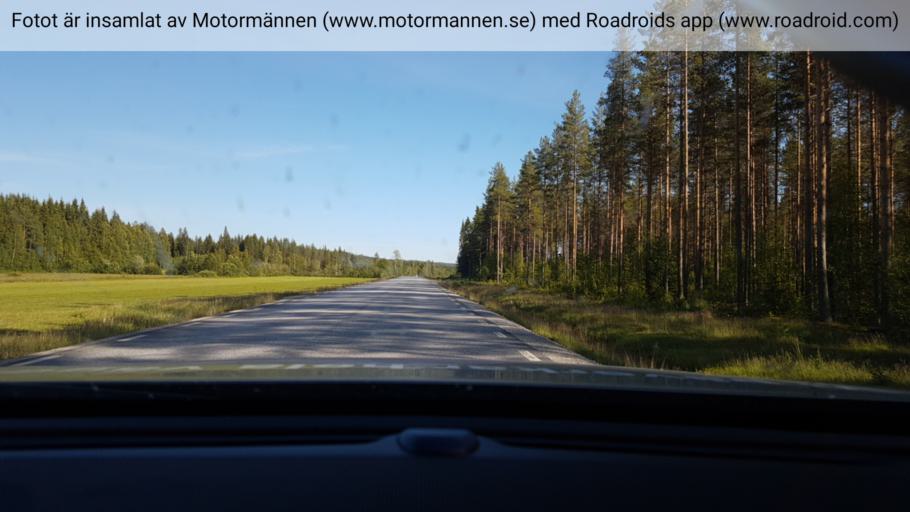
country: SE
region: Vaesterbotten
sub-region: Vindelns Kommun
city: Vindeln
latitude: 64.2004
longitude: 19.4504
